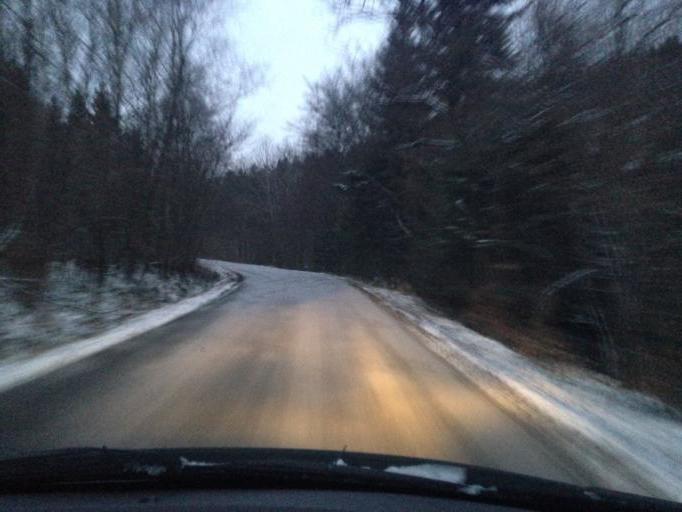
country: PL
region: Subcarpathian Voivodeship
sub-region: Powiat jasielski
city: Krempna
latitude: 49.5124
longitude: 21.5417
